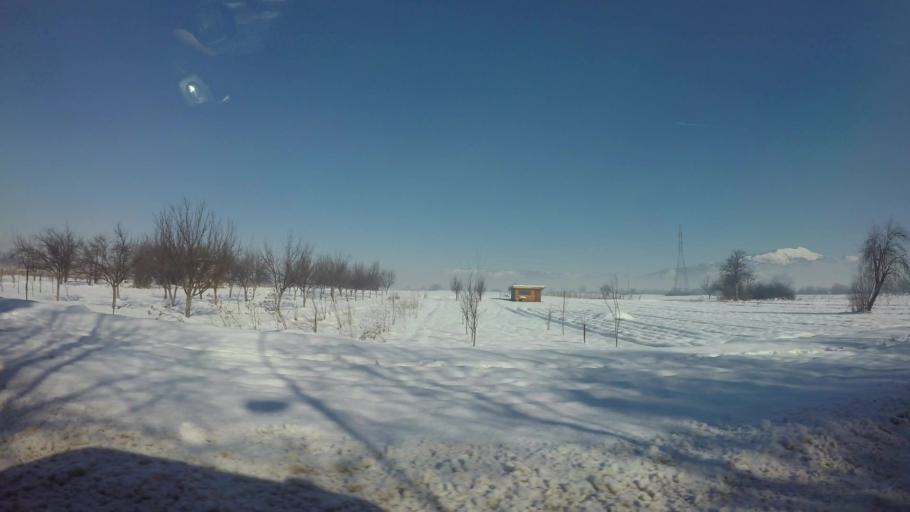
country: BA
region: Federation of Bosnia and Herzegovina
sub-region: Kanton Sarajevo
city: Sarajevo
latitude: 43.7950
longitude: 18.3233
